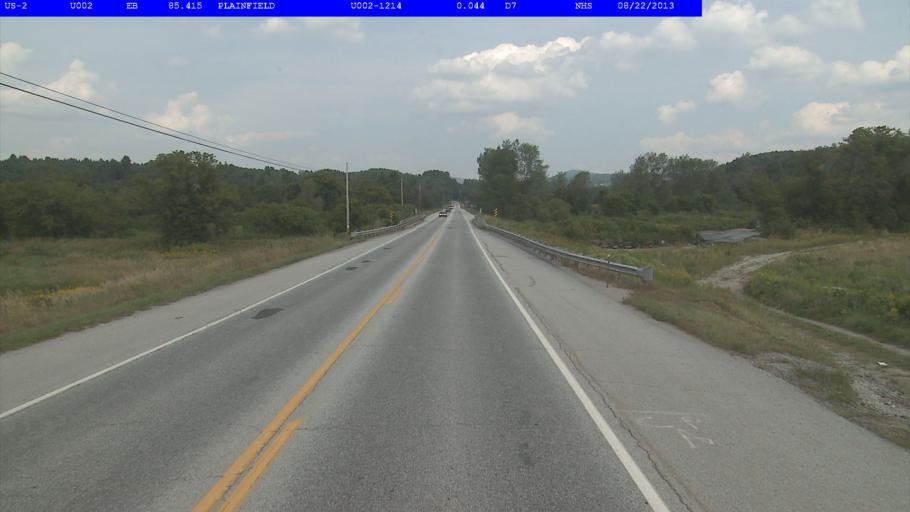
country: US
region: Vermont
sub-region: Washington County
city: Barre
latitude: 44.2741
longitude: -72.4488
